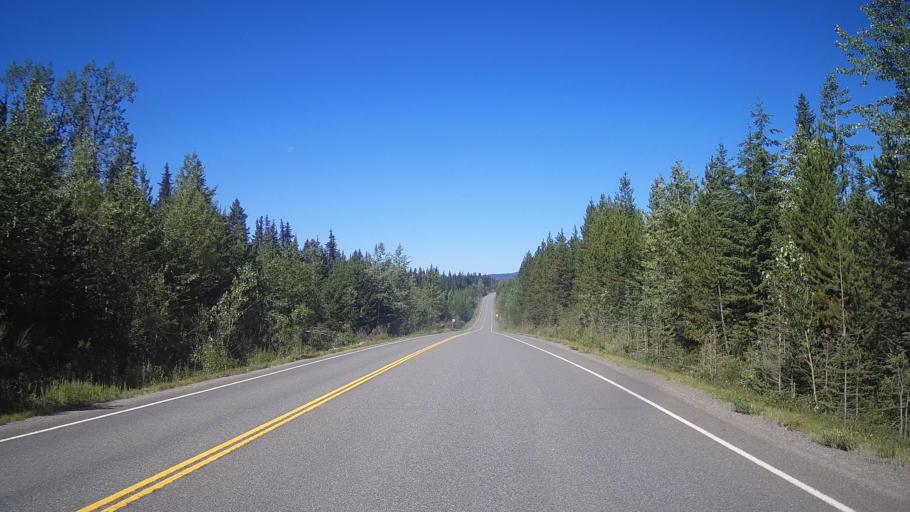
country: CA
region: British Columbia
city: Kamloops
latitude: 51.4971
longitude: -120.3787
